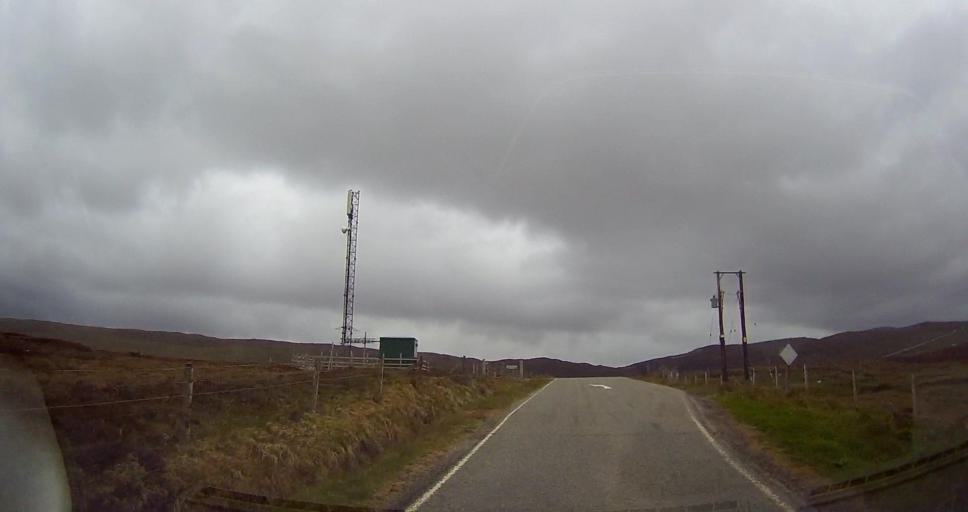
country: GB
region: Scotland
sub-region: Shetland Islands
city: Lerwick
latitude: 60.2769
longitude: -1.2625
